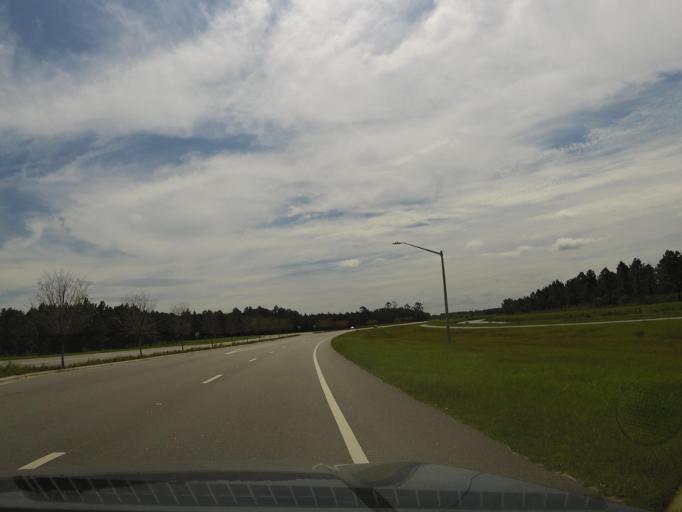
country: US
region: Florida
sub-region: Saint Johns County
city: Fruit Cove
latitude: 30.0141
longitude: -81.5081
